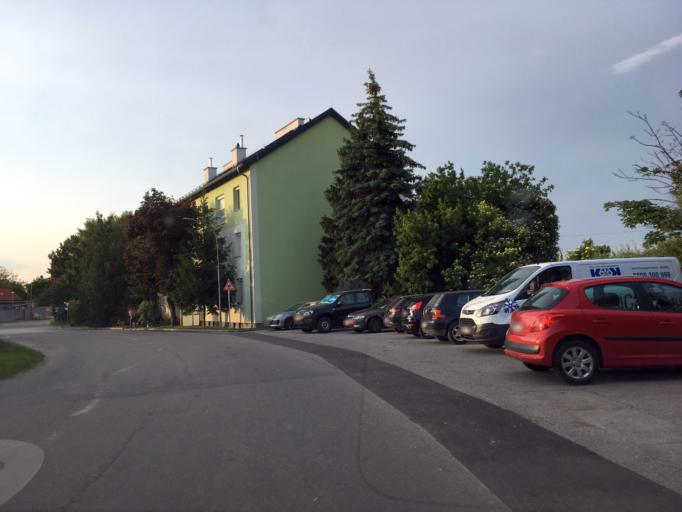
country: AT
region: Lower Austria
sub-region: Politischer Bezirk Wien-Umgebung
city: Gerasdorf bei Wien
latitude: 48.2997
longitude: 16.4731
